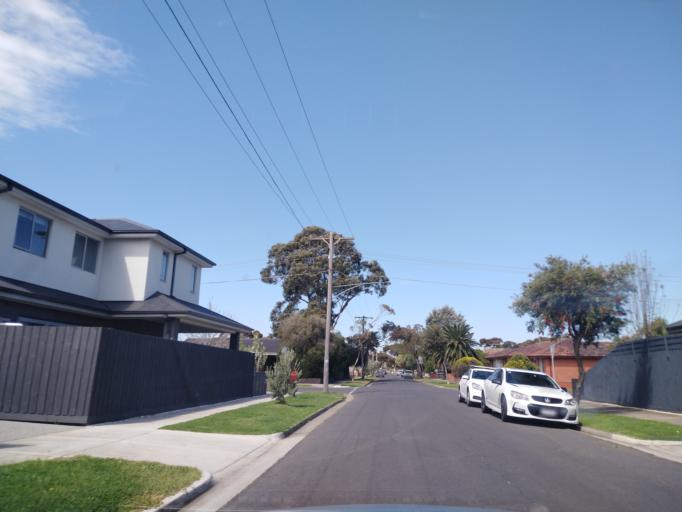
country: AU
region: Victoria
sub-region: Hobsons Bay
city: Altona North
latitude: -37.8331
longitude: 144.8521
